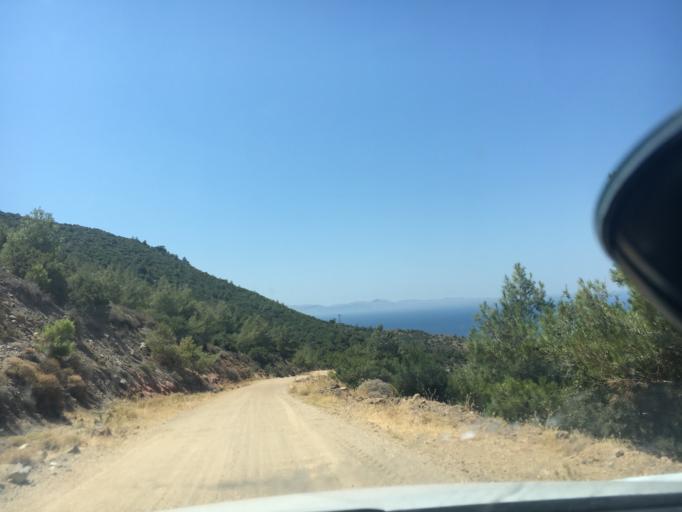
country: TR
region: Canakkale
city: Gulpinar
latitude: 39.4837
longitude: 26.0751
